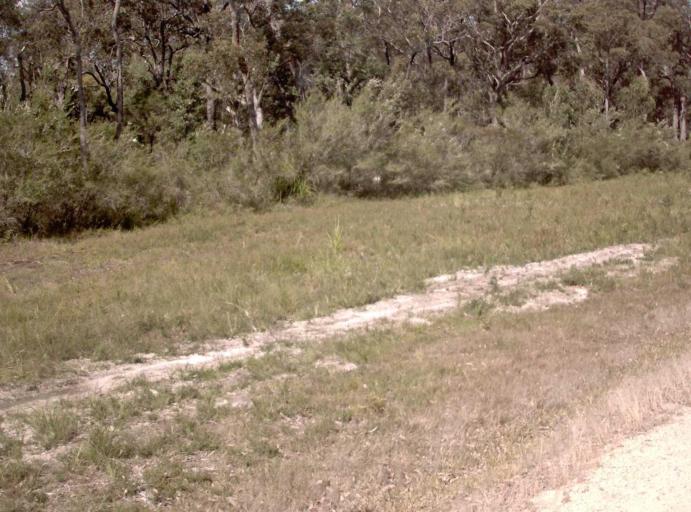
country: AU
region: New South Wales
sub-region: Bega Valley
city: Eden
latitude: -37.5464
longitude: 149.7216
